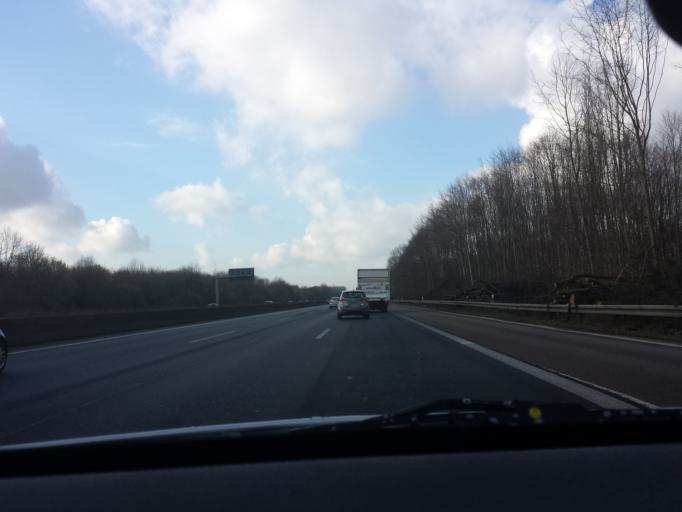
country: DE
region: North Rhine-Westphalia
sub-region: Regierungsbezirk Dusseldorf
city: Erkrath
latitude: 51.1921
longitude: 6.9106
